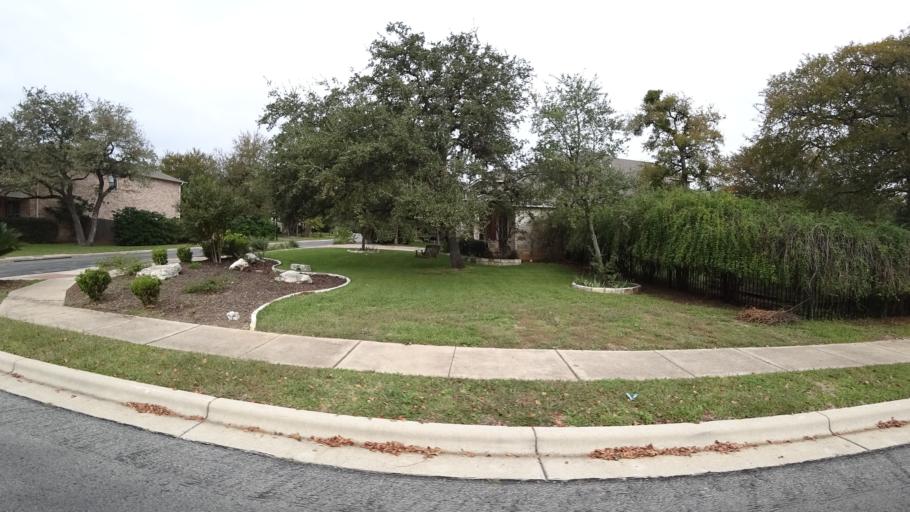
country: US
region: Texas
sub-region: Travis County
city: Shady Hollow
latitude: 30.1943
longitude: -97.9023
